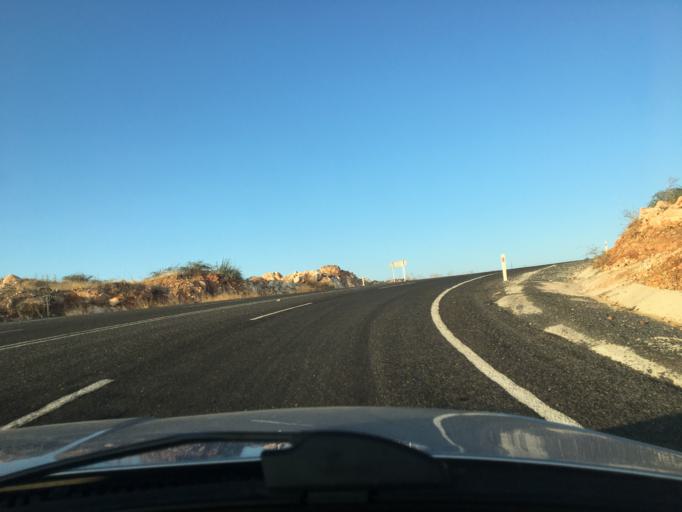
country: TR
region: Sanliurfa
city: Halfeti
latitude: 37.2404
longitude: 37.8827
